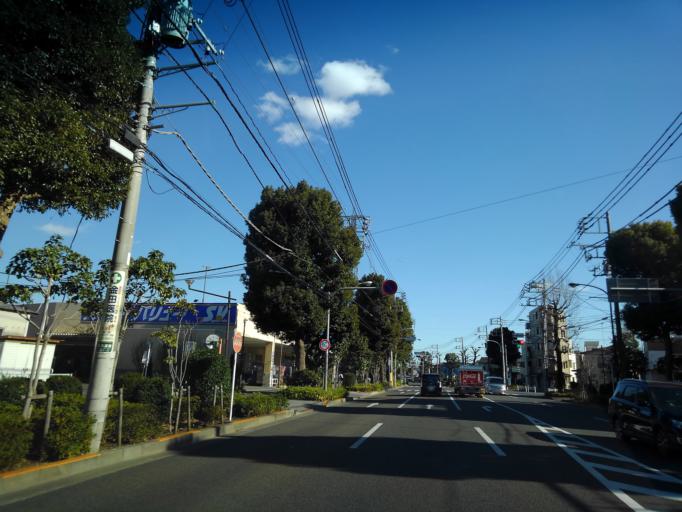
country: JP
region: Tokyo
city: Kokubunji
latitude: 35.6880
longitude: 139.4895
